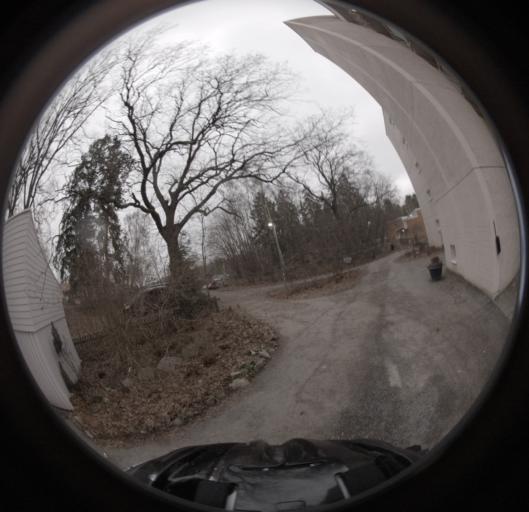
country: SE
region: Stockholm
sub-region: Upplands Vasby Kommun
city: Upplands Vaesby
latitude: 59.4856
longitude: 17.9345
